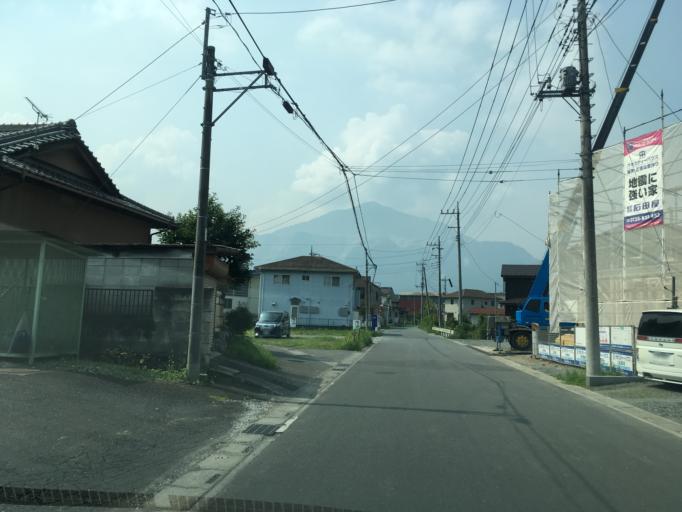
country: JP
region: Saitama
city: Chichibu
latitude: 35.9984
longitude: 139.1062
